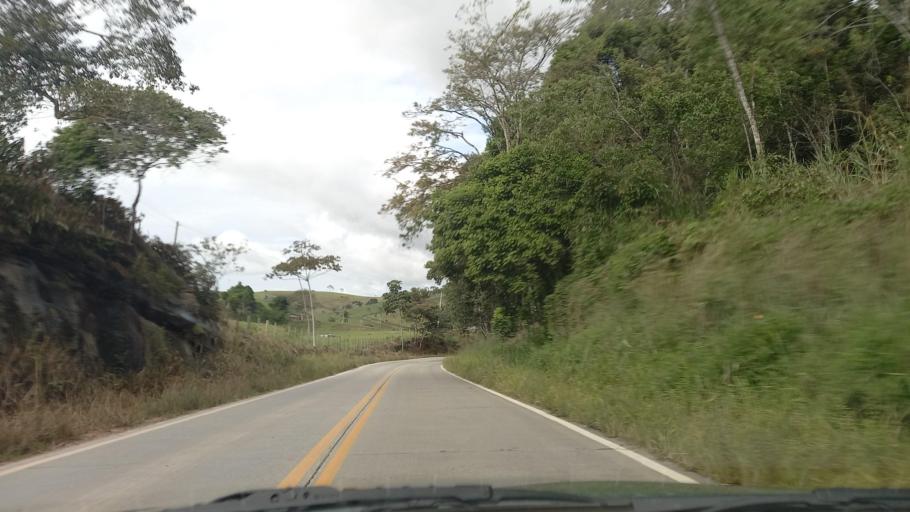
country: BR
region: Pernambuco
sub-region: Maraial
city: Maraial
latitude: -8.7804
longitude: -35.9155
